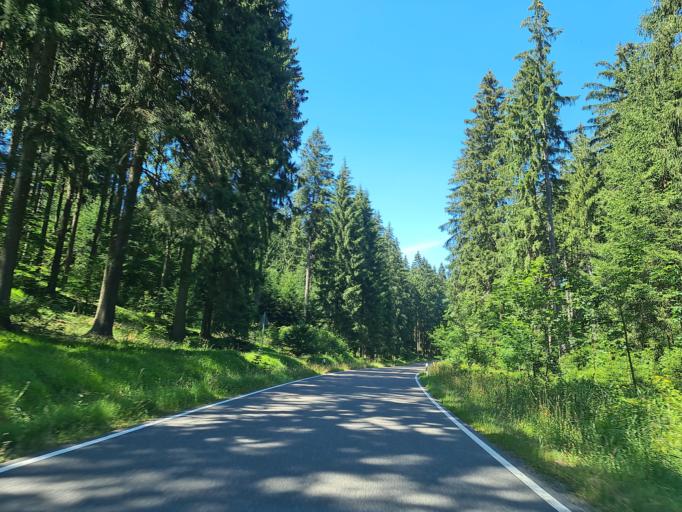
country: DE
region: Saxony
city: Rechenberg-Bienenmuhle
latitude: 50.7106
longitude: 13.5421
